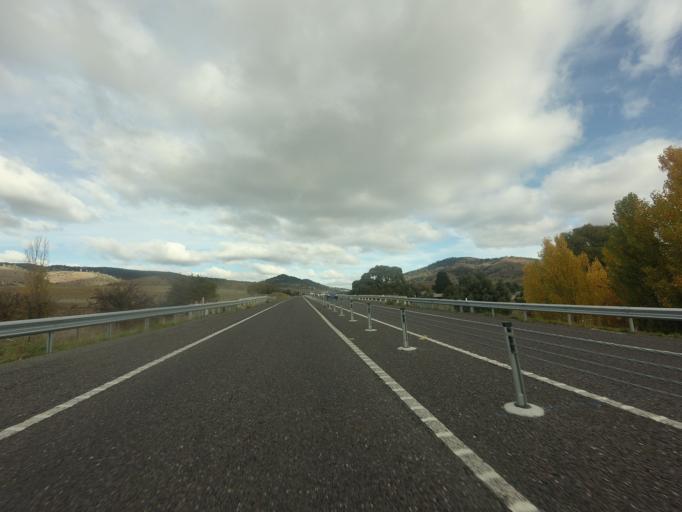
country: AU
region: Tasmania
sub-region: Brighton
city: Bridgewater
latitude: -42.5286
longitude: 147.2024
